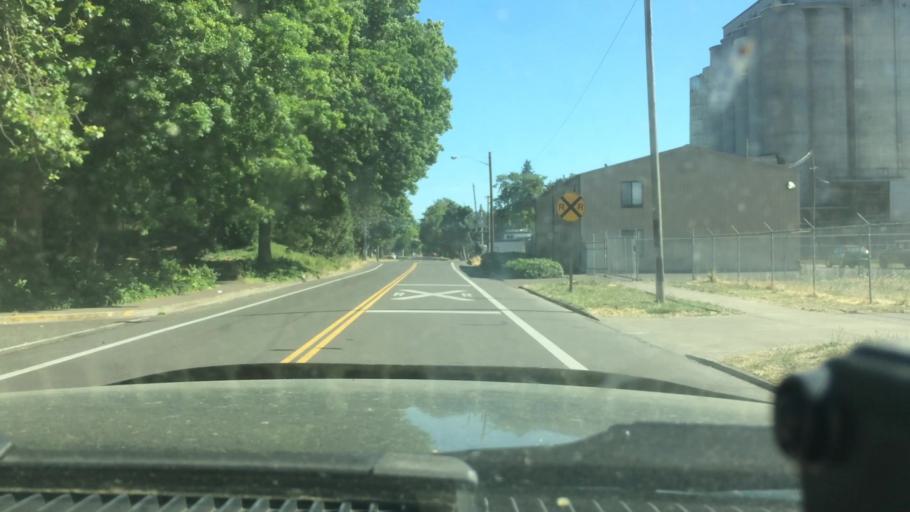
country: US
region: Oregon
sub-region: Lane County
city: Eugene
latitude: 44.0574
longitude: -123.1019
